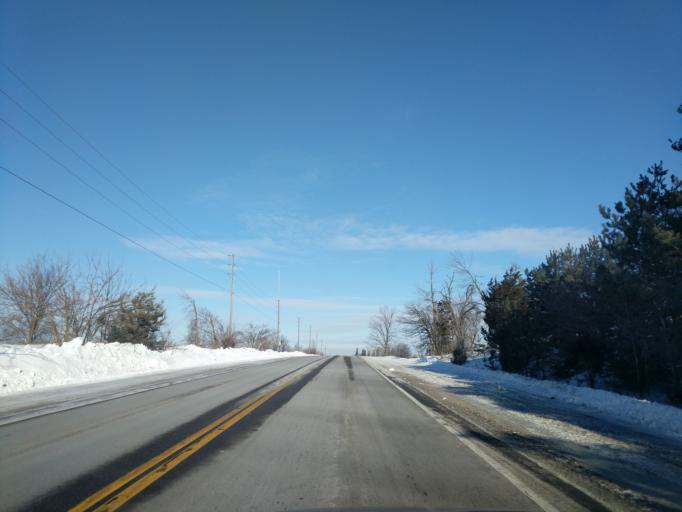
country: CA
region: Ontario
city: Pickering
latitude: 43.8540
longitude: -79.1524
